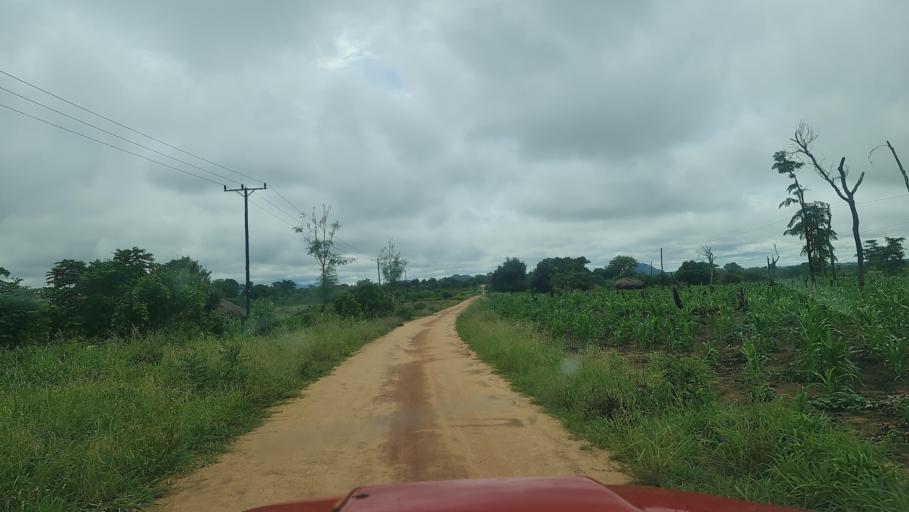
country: MW
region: Southern Region
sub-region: Nsanje District
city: Nsanje
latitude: -17.1781
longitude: 35.9019
